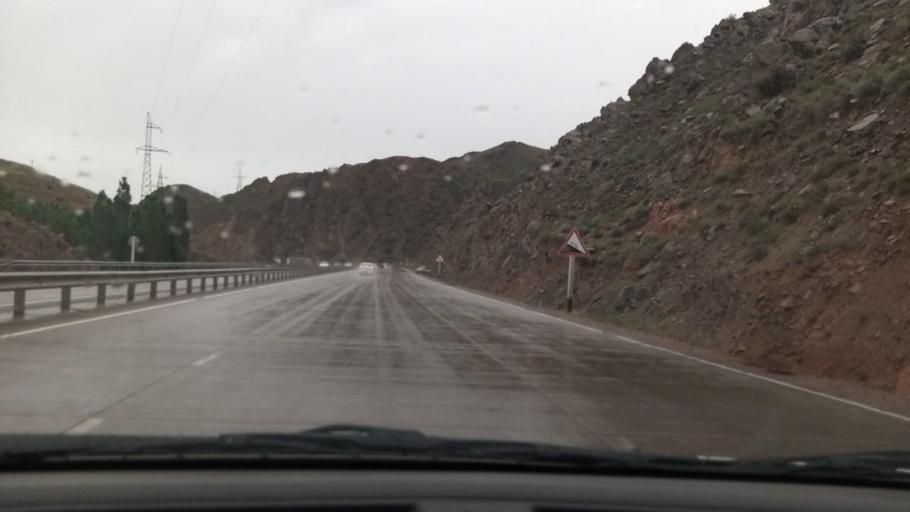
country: TJ
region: Viloyati Sughd
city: Shaydon
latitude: 40.9592
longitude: 70.6664
